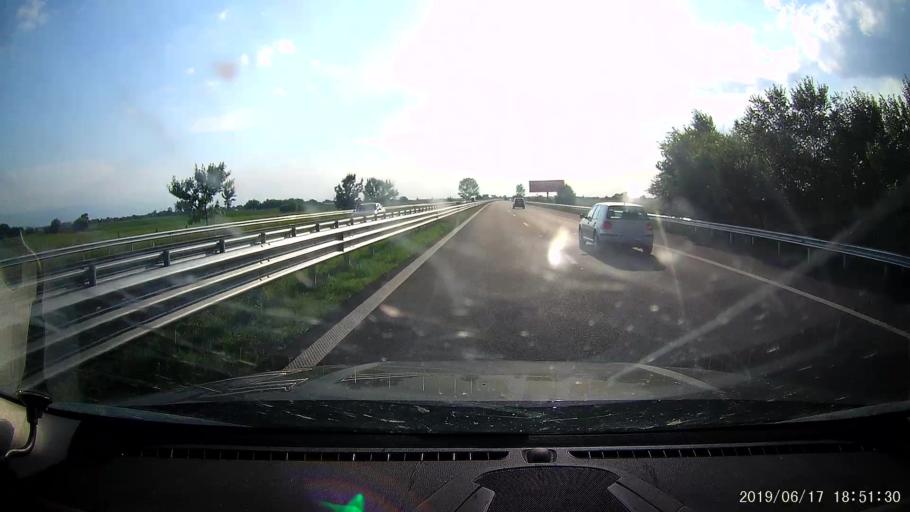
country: BG
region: Plovdiv
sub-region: Obshtina Rakovski
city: Rakovski
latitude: 42.2137
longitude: 24.9694
